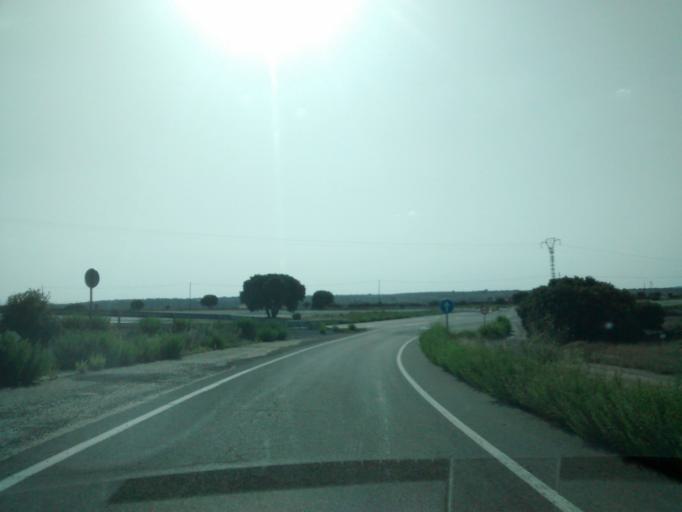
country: ES
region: Castille-La Mancha
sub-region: Provincia de Guadalajara
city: Sauca
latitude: 41.0259
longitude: -2.5185
